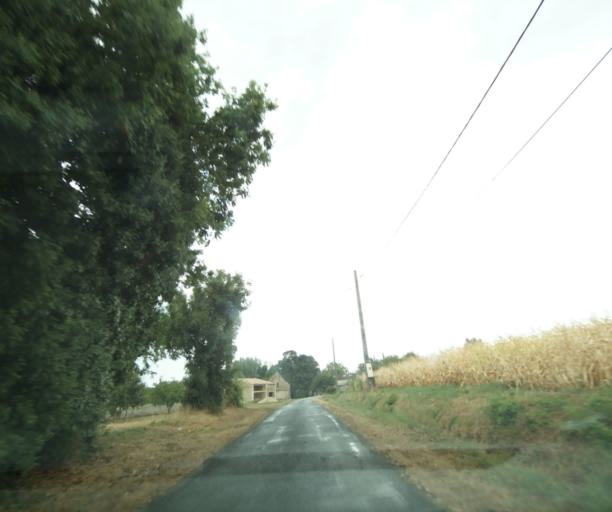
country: FR
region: Poitou-Charentes
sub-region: Departement de la Charente-Maritime
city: Tonnay-Charente
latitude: 45.9447
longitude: -0.8718
